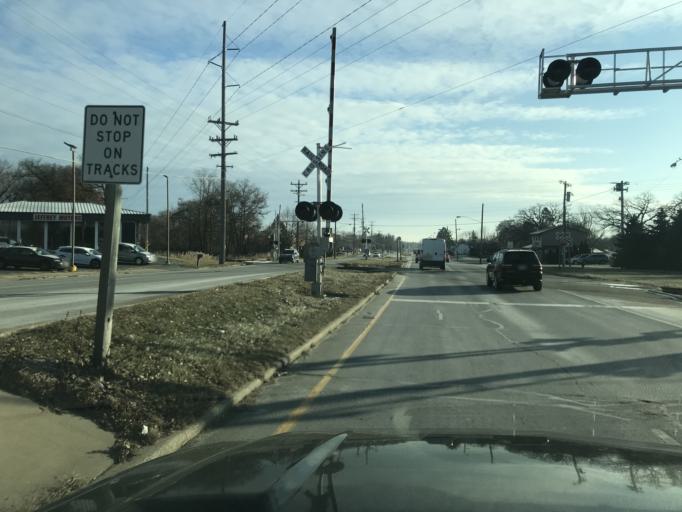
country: US
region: Wisconsin
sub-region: Kenosha County
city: Kenosha
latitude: 42.5662
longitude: -87.8693
